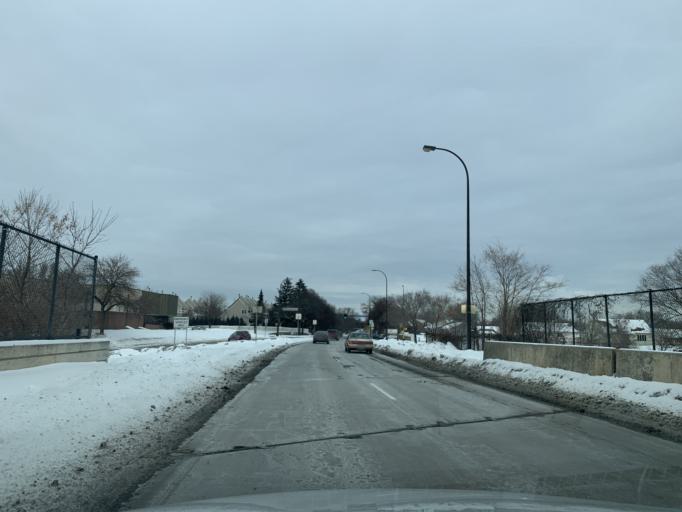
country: US
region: Minnesota
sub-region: Hennepin County
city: Minneapolis
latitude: 44.9908
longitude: -93.2879
